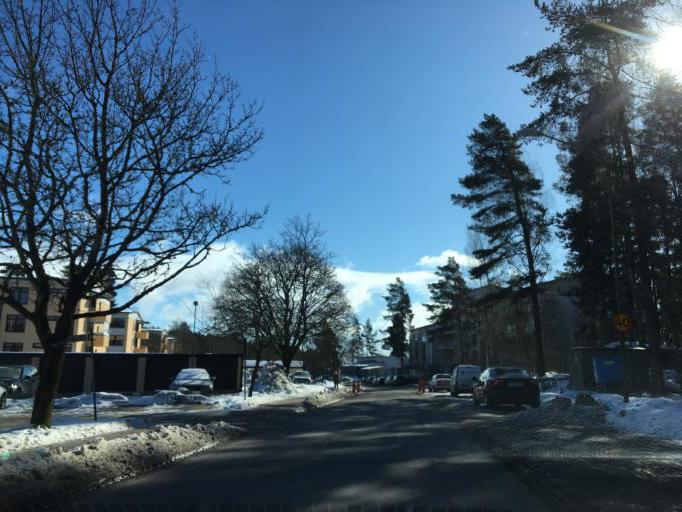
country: SE
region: Vaestmanland
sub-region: Vasteras
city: Vasteras
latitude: 59.6107
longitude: 16.5073
